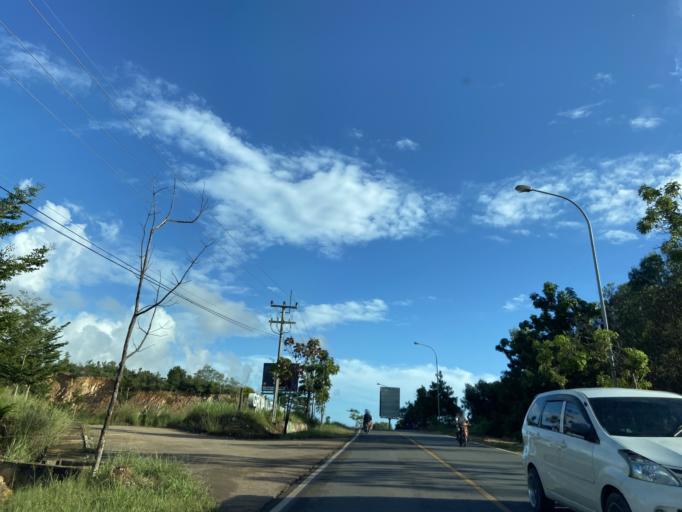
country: SG
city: Singapore
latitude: 1.0123
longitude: 104.0205
